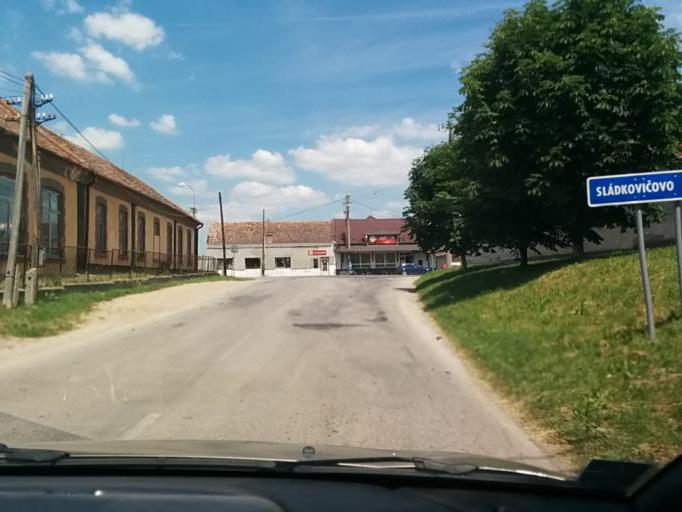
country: SK
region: Trnavsky
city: Sladkovicovo
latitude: 48.2307
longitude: 17.5696
